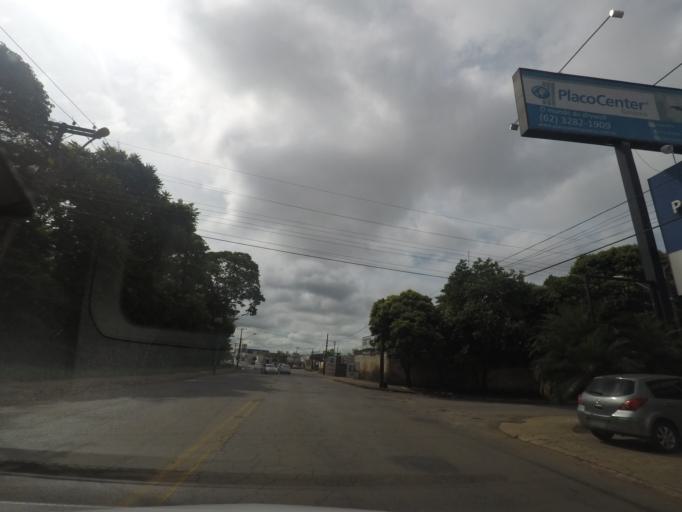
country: BR
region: Goias
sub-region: Goiania
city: Goiania
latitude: -16.7271
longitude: -49.2466
